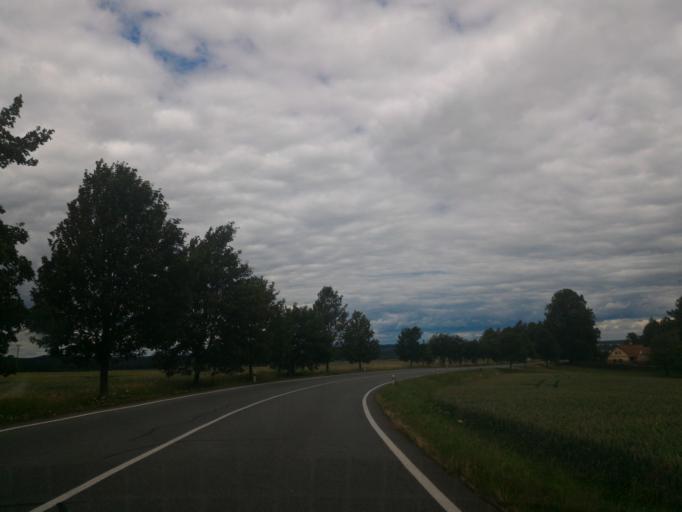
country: CZ
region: Vysocina
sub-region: Okres Pelhrimov
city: Zeliv
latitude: 49.4840
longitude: 15.1794
